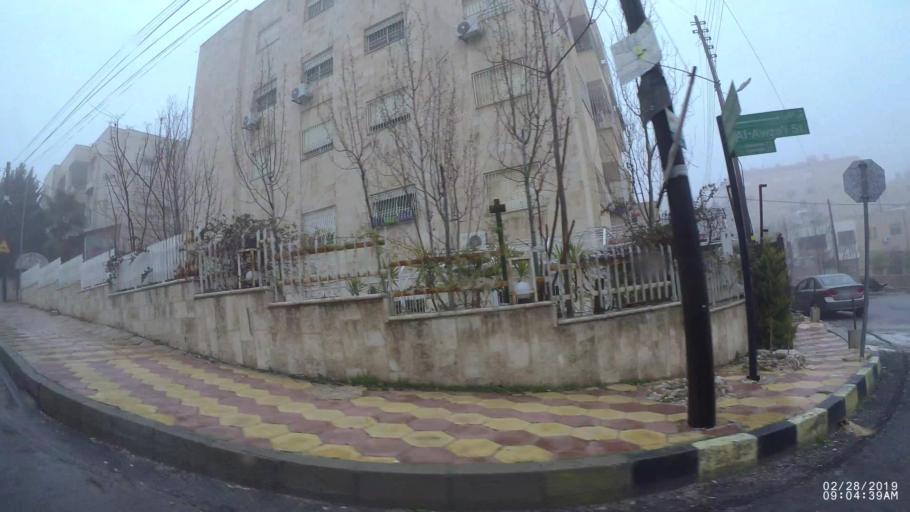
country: JO
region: Amman
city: Al Jubayhah
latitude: 32.0178
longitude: 35.8771
